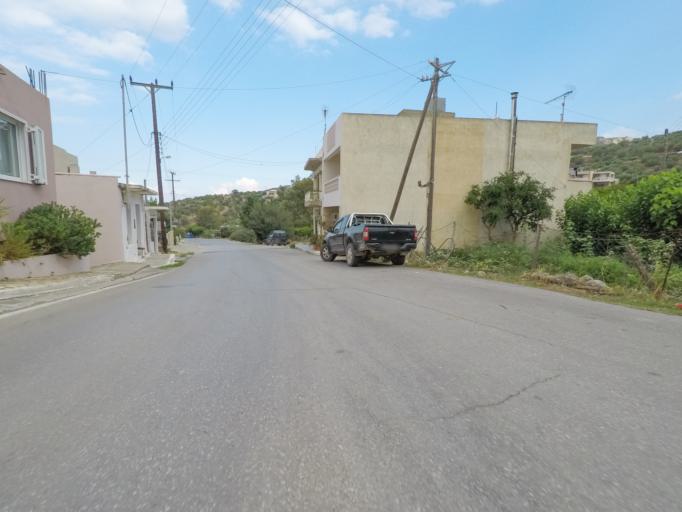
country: GR
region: Crete
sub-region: Nomos Lasithiou
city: Kritsa
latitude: 35.1548
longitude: 25.6483
